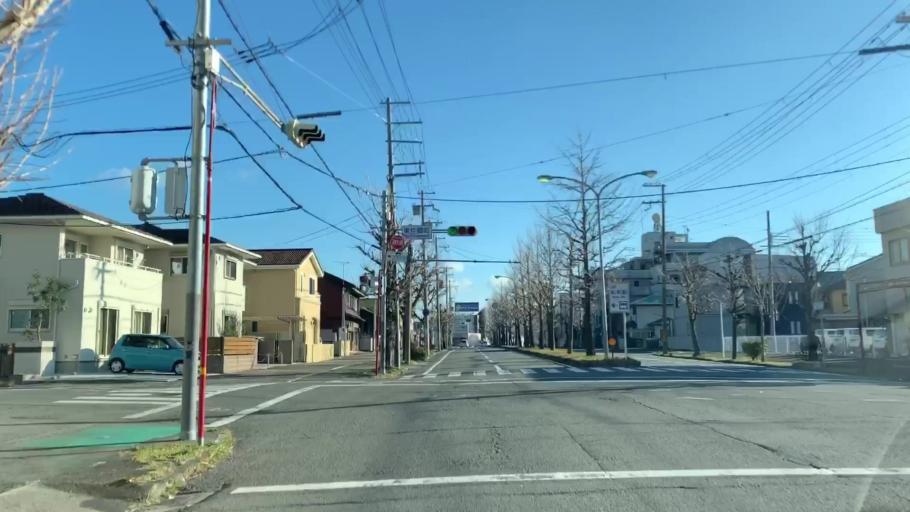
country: JP
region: Wakayama
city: Wakayama-shi
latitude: 34.2390
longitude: 135.1793
